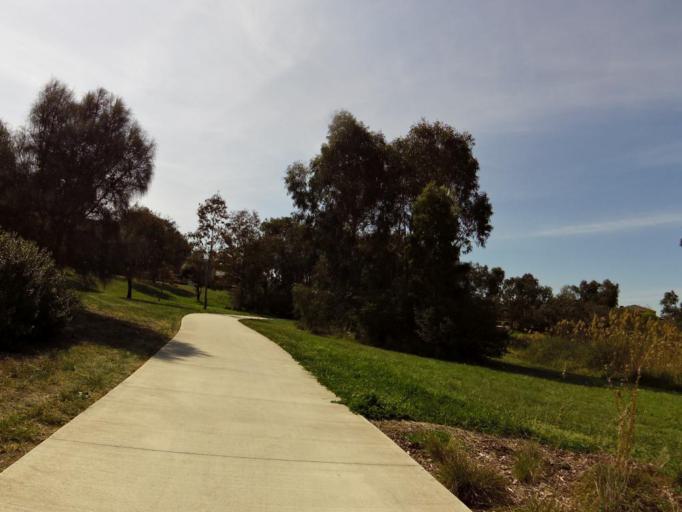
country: AU
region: Victoria
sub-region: Brimbank
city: Deer Park
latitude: -37.7646
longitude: 144.7776
